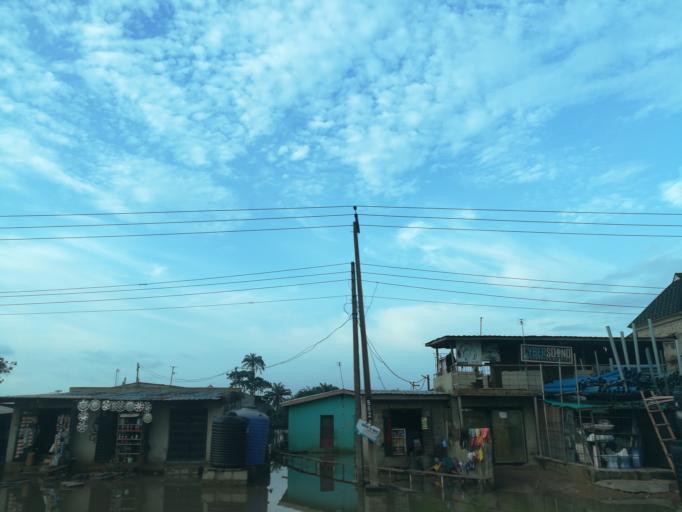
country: NG
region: Lagos
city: Ojota
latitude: 6.6097
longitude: 3.4226
